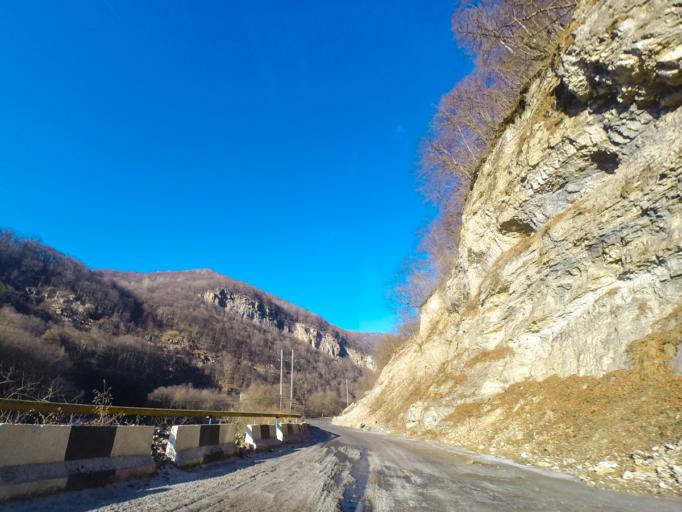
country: RU
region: Kabardino-Balkariya
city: Zhankhoteko
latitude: 43.4646
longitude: 43.2581
